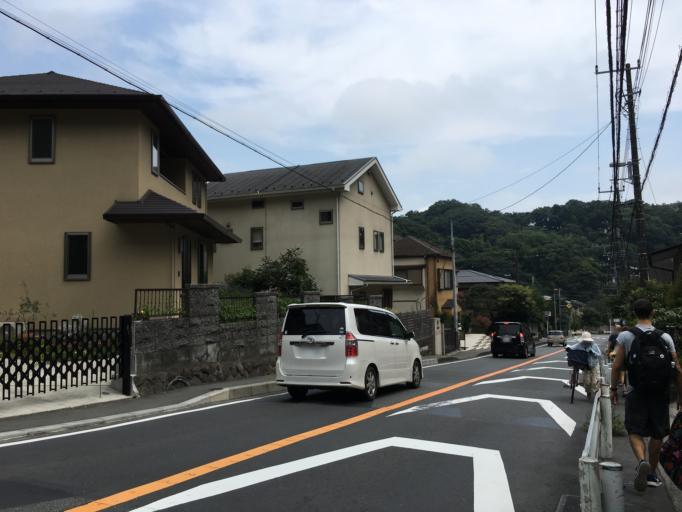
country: JP
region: Kanagawa
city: Kamakura
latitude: 35.3287
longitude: 139.5547
